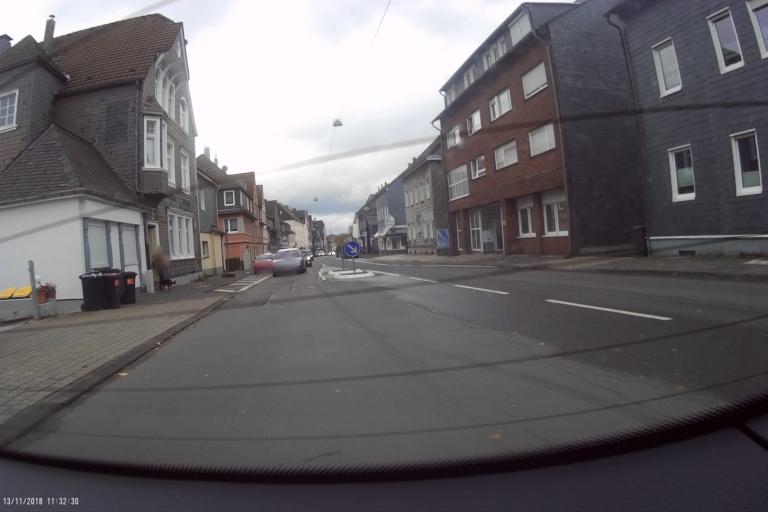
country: DE
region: North Rhine-Westphalia
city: Wermelskirchen
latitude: 51.1838
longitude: 7.2543
